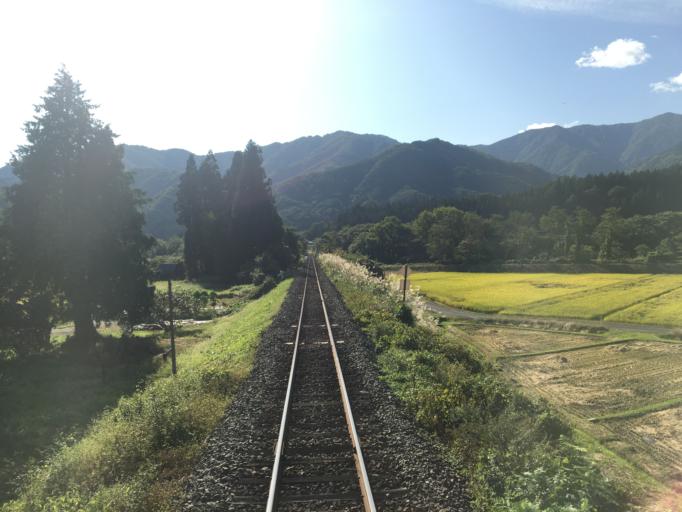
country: JP
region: Akita
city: Kakunodatemachi
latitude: 39.7276
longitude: 140.5647
